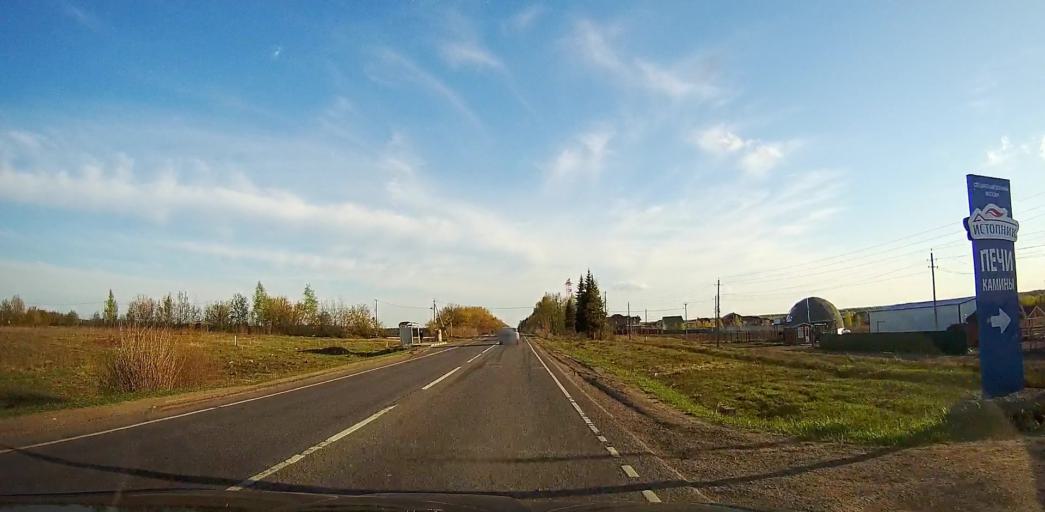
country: RU
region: Moskovskaya
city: Bronnitsy
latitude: 55.3203
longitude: 38.2179
